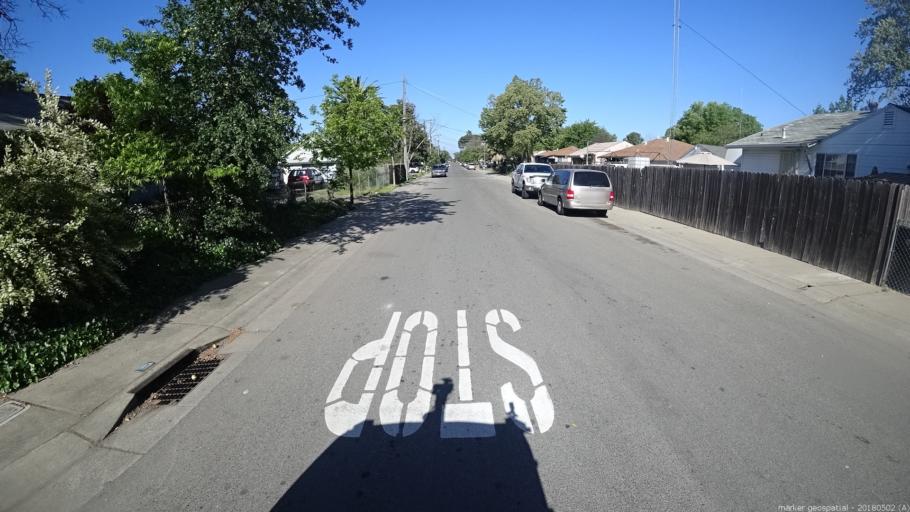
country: US
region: California
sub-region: Sacramento County
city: Arden-Arcade
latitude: 38.6184
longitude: -121.4209
